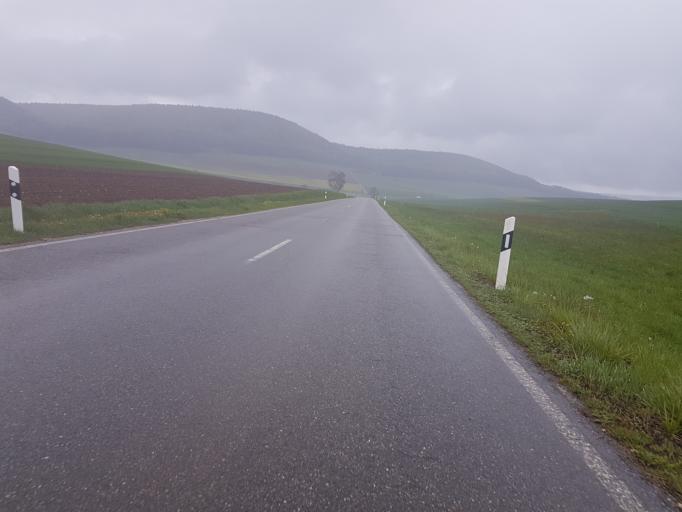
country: DE
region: Baden-Wuerttemberg
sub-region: Freiburg Region
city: Blumberg
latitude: 47.8846
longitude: 8.5559
